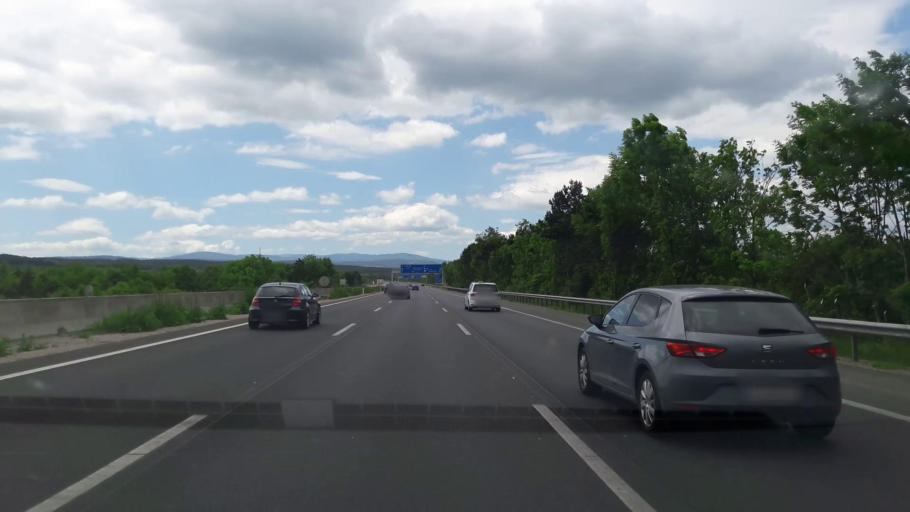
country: AT
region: Lower Austria
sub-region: Politischer Bezirk Neunkirchen
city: Breitenau
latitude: 47.7252
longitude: 16.1454
